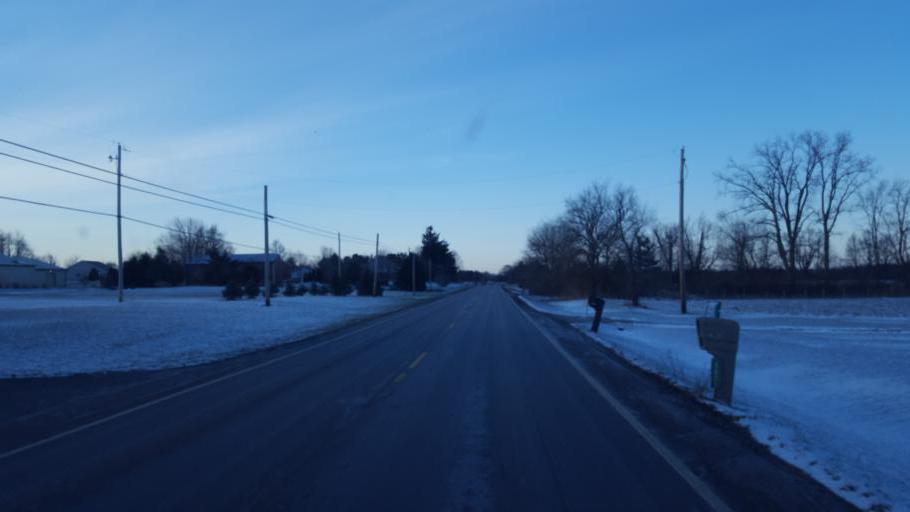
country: US
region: Ohio
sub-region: Morrow County
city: Mount Gilead
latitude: 40.5261
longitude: -82.8341
